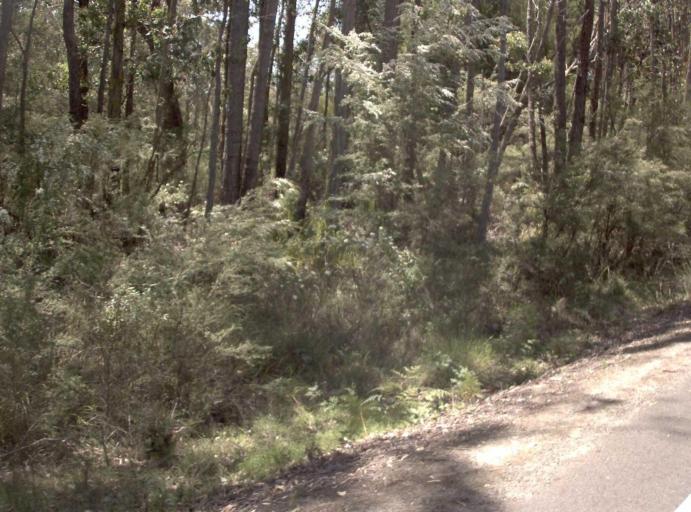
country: AU
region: Victoria
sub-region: East Gippsland
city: Lakes Entrance
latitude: -37.7325
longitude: 148.1070
